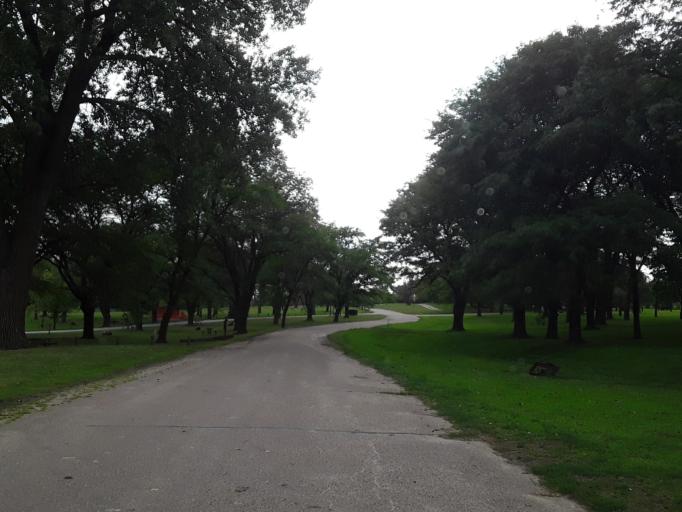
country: US
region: Nebraska
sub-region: Saunders County
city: Ashland
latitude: 41.1027
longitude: -96.4392
